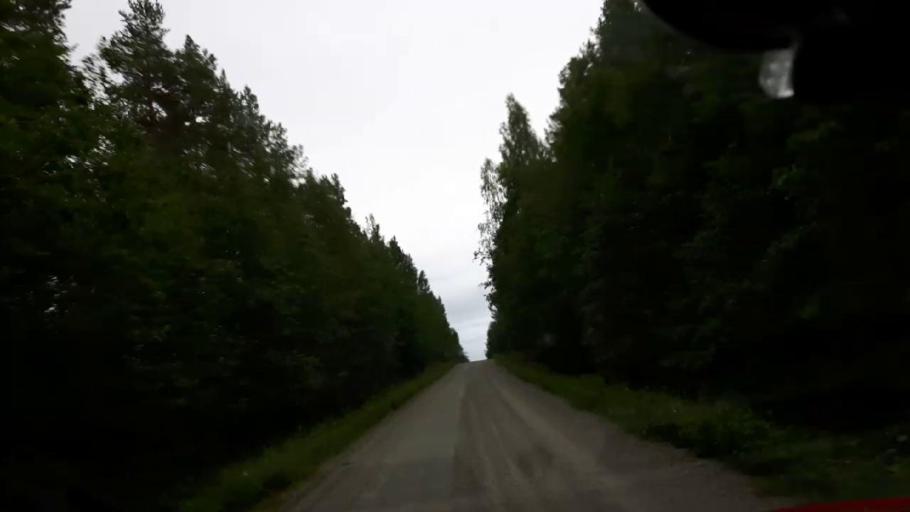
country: SE
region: Vaesternorrland
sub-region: Ange Kommun
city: Ange
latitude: 62.7910
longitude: 15.7733
